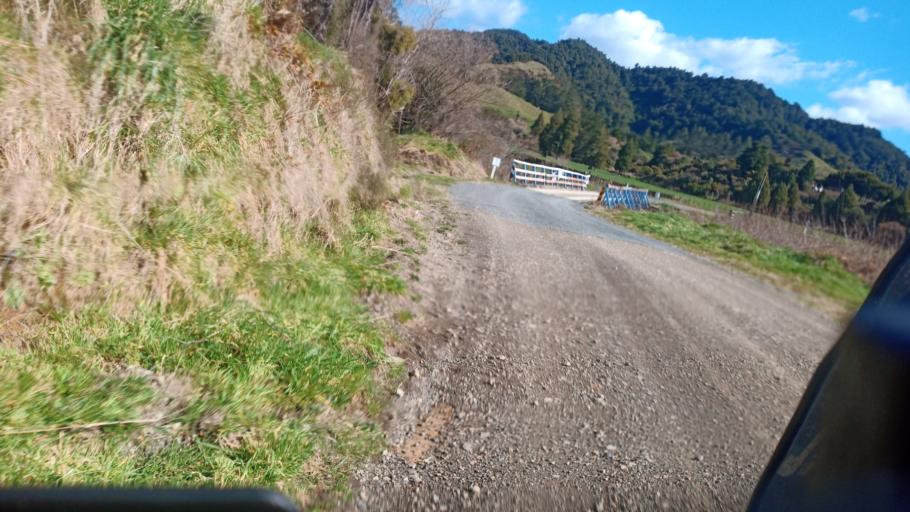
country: NZ
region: Bay of Plenty
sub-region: Opotiki District
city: Opotiki
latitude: -38.1118
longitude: 177.5137
